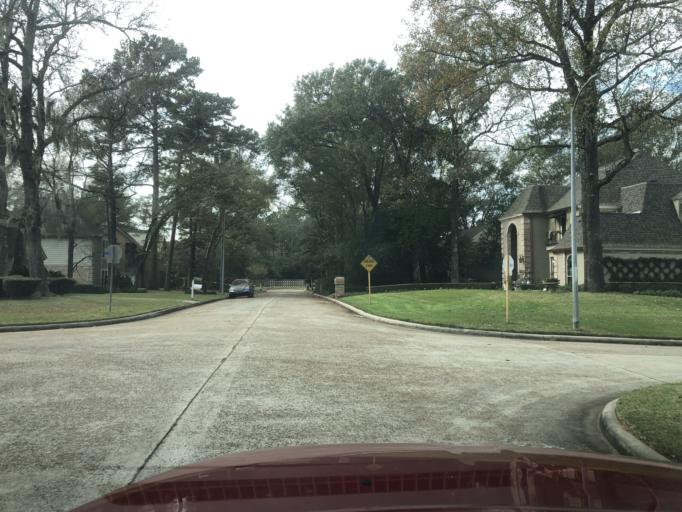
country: US
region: Texas
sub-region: Harris County
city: Spring
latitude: 30.0185
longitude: -95.4661
